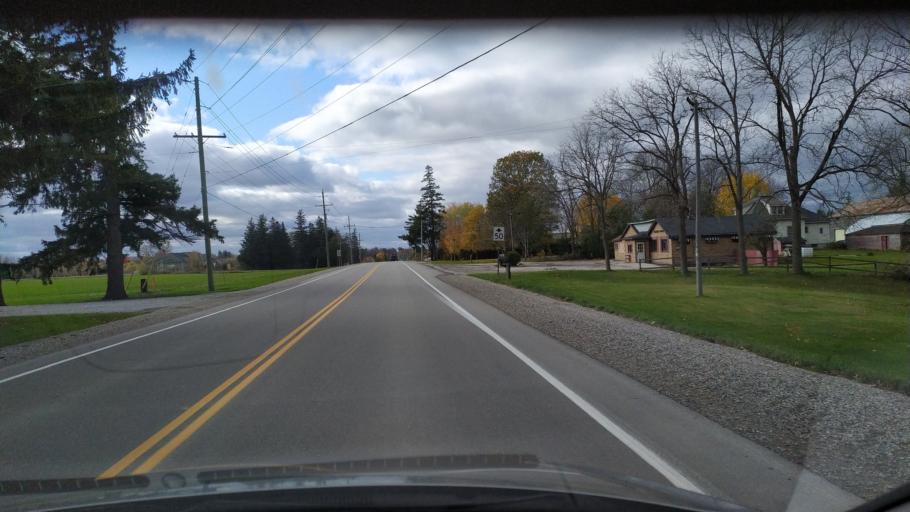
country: CA
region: Ontario
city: Stratford
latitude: 43.2633
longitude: -81.1087
